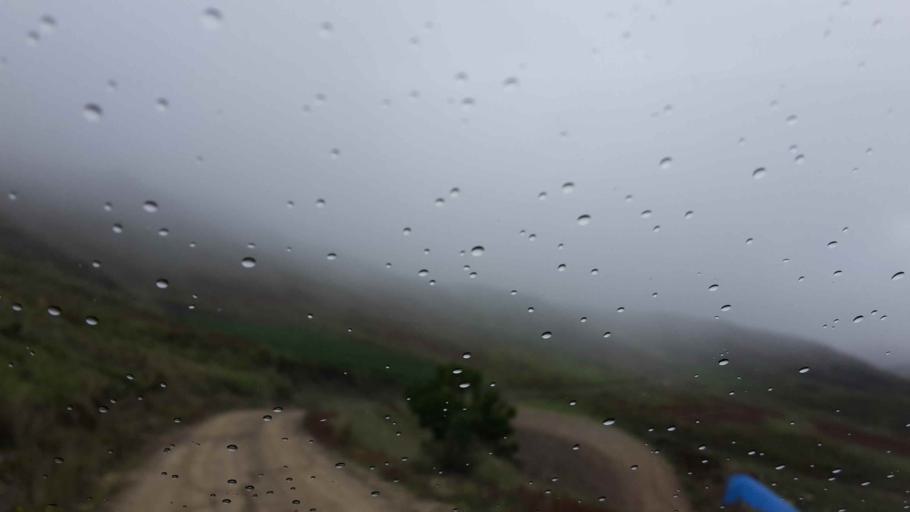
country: BO
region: Cochabamba
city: Cochabamba
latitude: -17.1511
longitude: -66.1058
